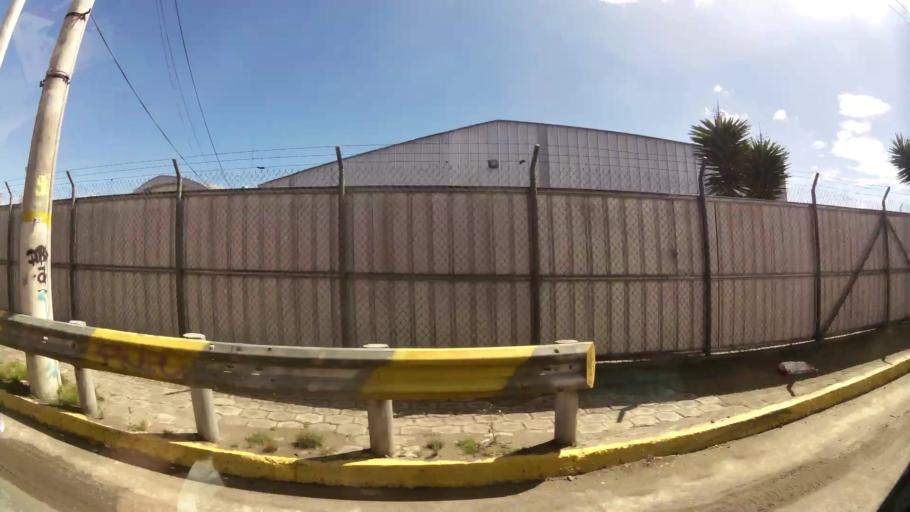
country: EC
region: Pichincha
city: Quito
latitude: -0.3033
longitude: -78.5482
